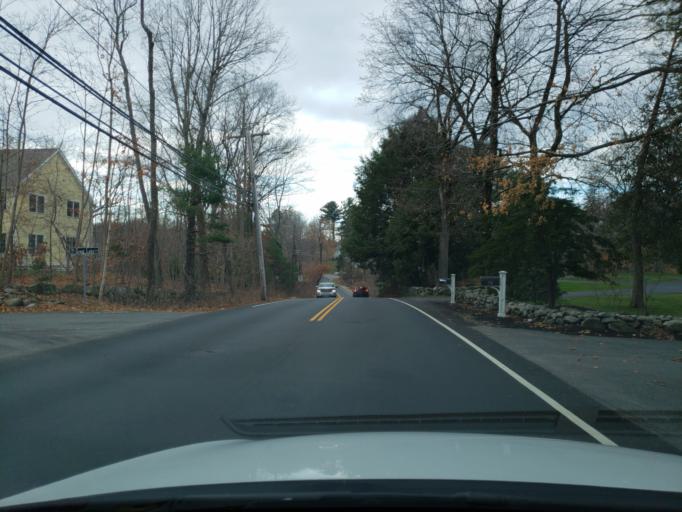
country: US
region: Massachusetts
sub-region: Essex County
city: North Andover
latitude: 42.6854
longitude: -71.1085
